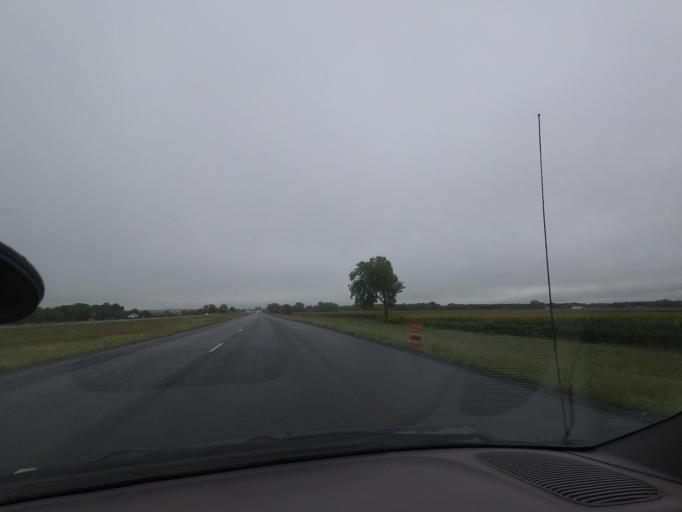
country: US
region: Illinois
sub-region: Macon County
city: Harristown
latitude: 39.8315
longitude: -89.0833
